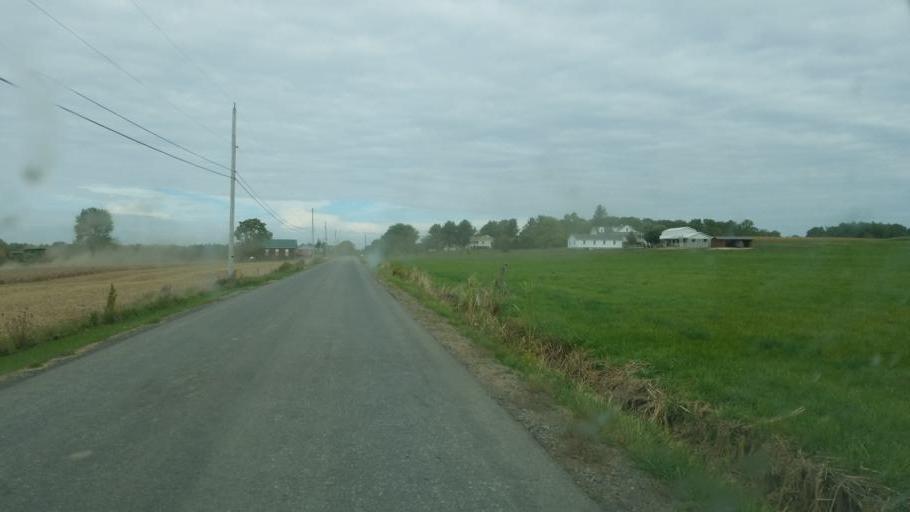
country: US
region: Pennsylvania
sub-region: Mercer County
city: Stoneboro
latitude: 41.3808
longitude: -80.2438
